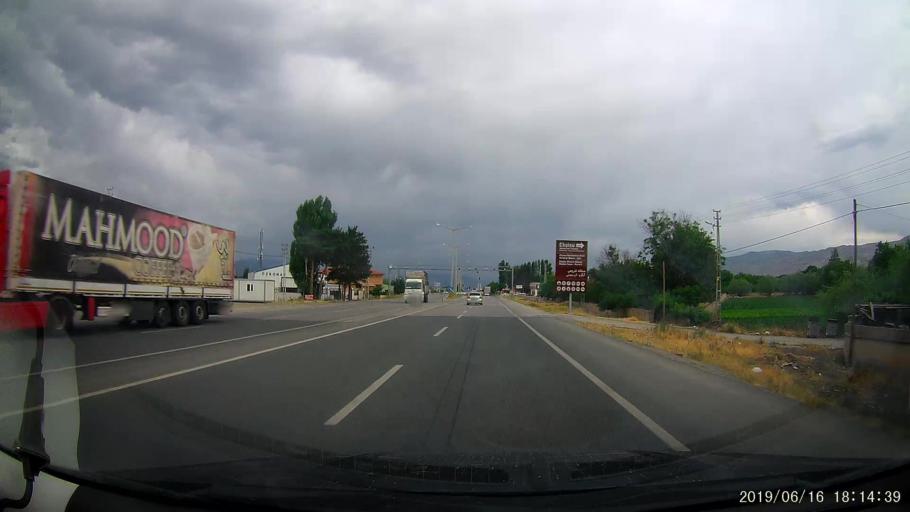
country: TR
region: Erzincan
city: Erzincan
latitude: 39.7255
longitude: 39.5551
